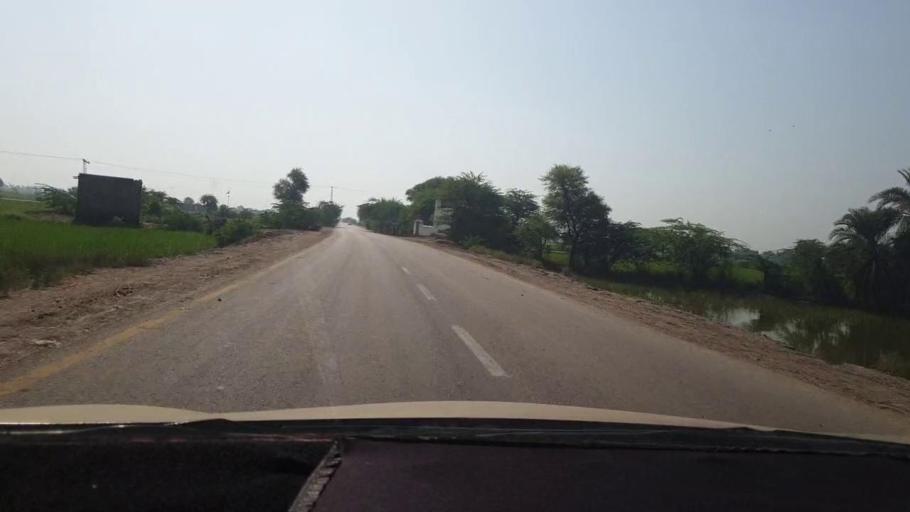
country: PK
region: Sindh
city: Miro Khan
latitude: 27.7220
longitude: 68.1420
